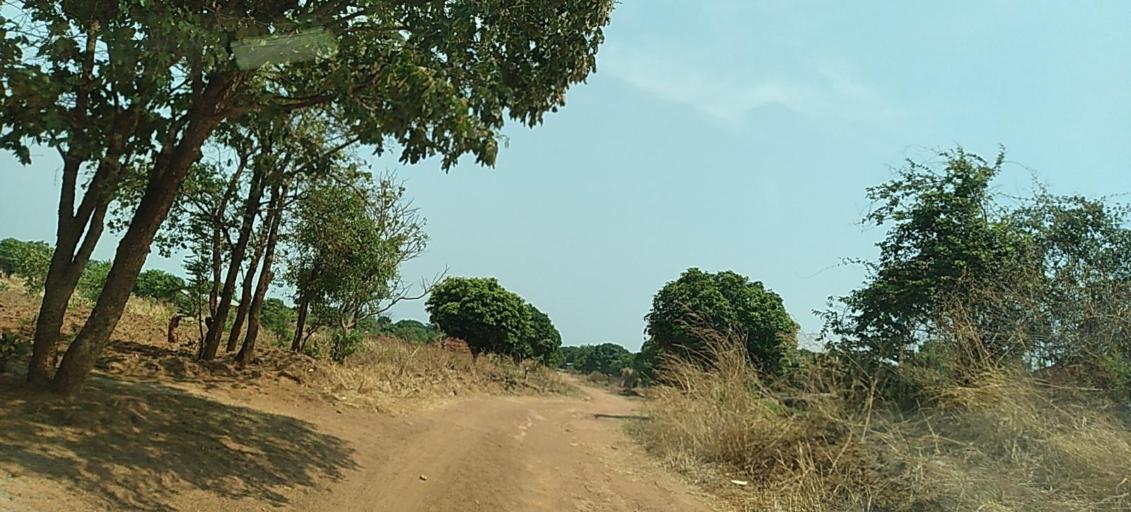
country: ZM
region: Copperbelt
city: Ndola
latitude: -13.0781
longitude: 28.7471
